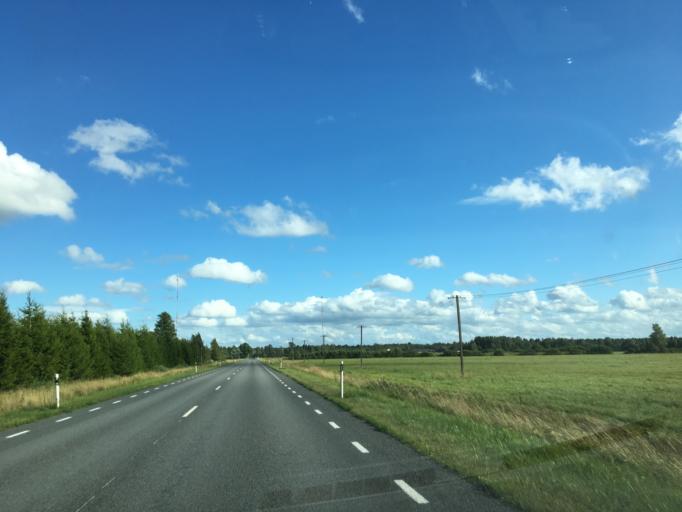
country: EE
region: Paernumaa
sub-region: Vaendra vald (alev)
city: Vandra
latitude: 58.5815
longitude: 25.1818
